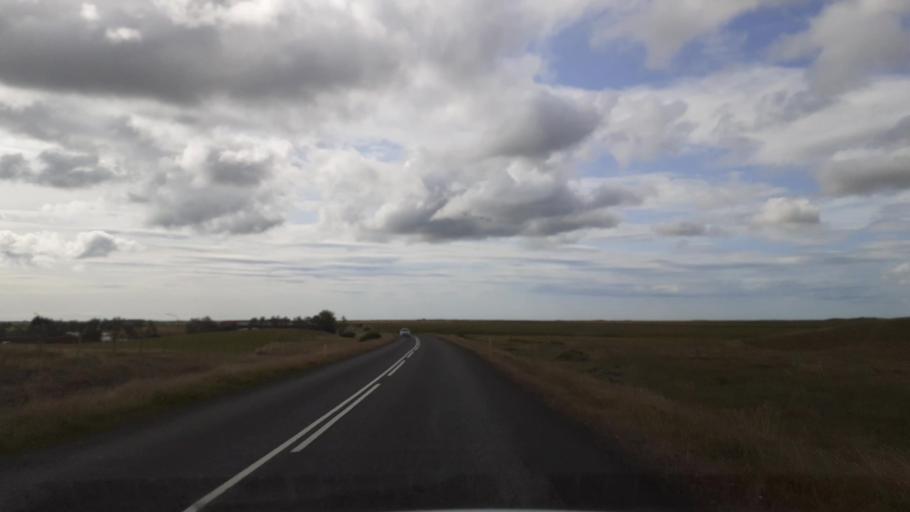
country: IS
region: South
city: Vestmannaeyjar
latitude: 63.8344
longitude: -20.4189
